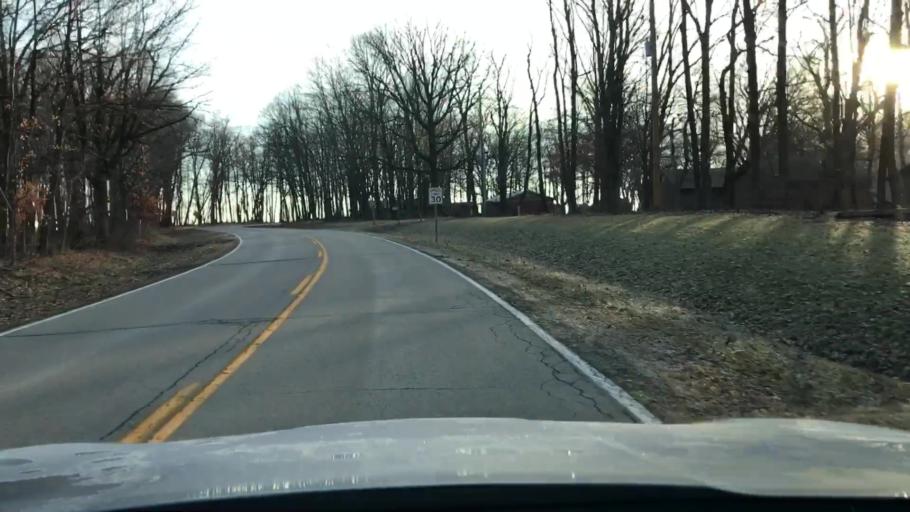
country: US
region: Illinois
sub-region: McLean County
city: Hudson
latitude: 40.6486
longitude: -88.9117
